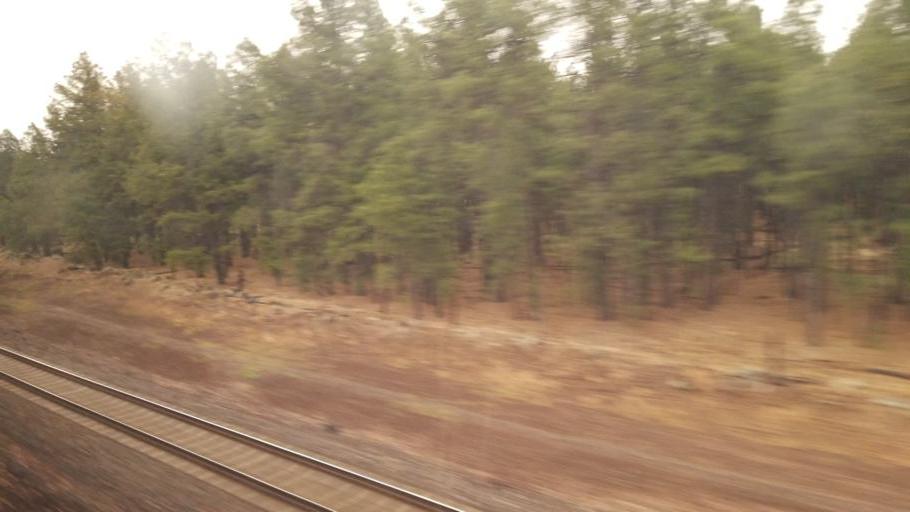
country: US
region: Arizona
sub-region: Coconino County
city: Parks
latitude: 35.2394
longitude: -111.9952
